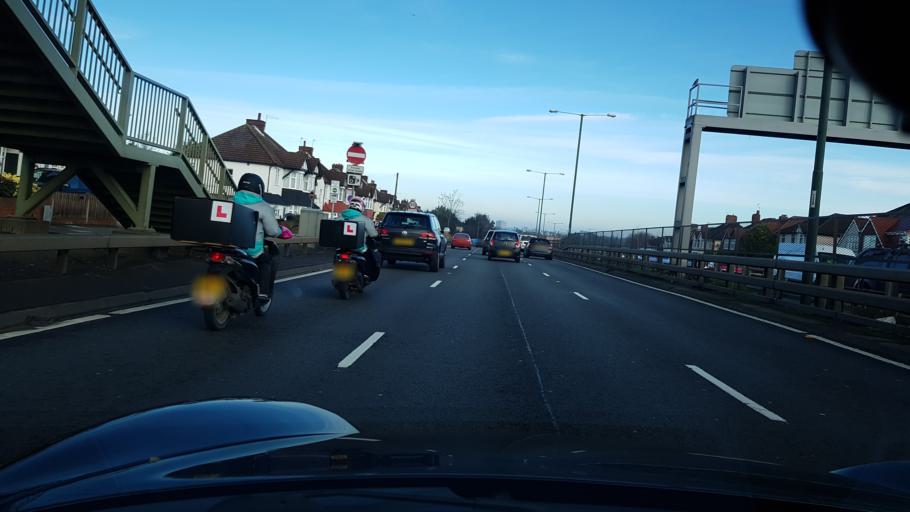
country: GB
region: England
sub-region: Greater London
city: New Malden
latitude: 51.3852
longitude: -0.2746
